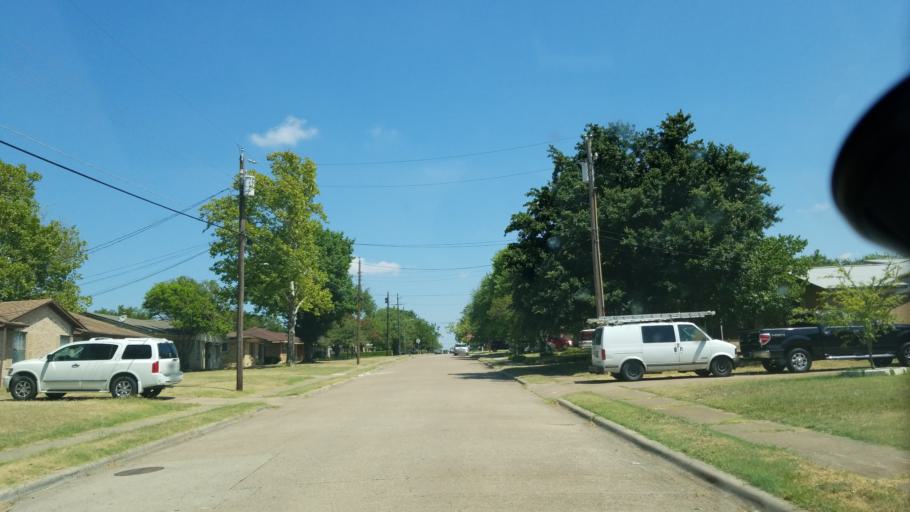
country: US
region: Texas
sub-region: Dallas County
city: Duncanville
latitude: 32.6569
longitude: -96.8993
